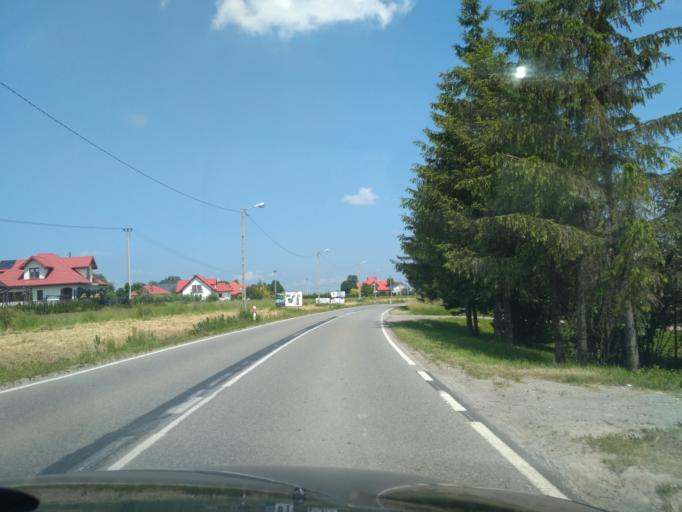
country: PL
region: Subcarpathian Voivodeship
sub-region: Powiat lancucki
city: Albigowa
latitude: 50.0239
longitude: 22.2245
